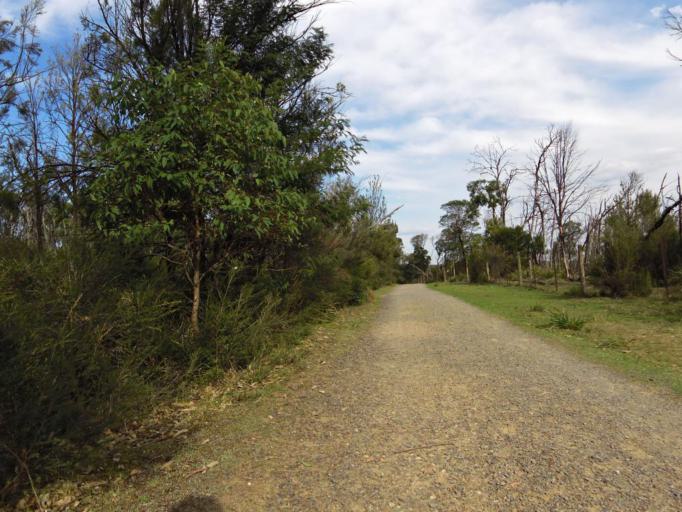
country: AU
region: Victoria
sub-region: Yarra Ranges
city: Lysterfield
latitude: -37.9541
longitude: 145.2978
